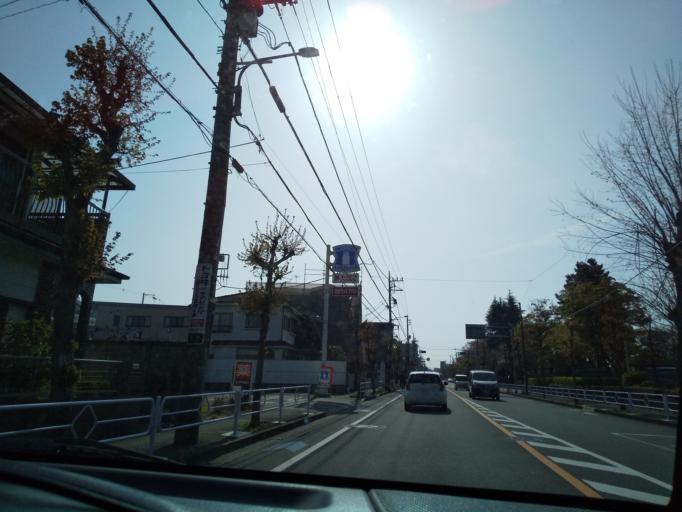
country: JP
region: Tokyo
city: Hino
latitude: 35.7005
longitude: 139.3923
